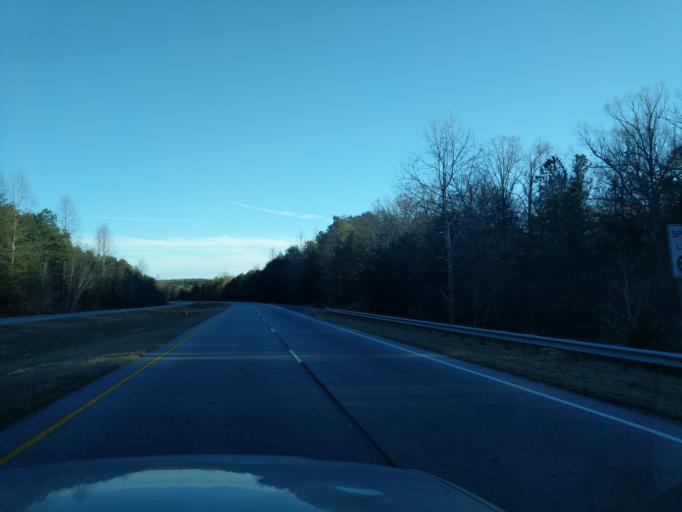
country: US
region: Georgia
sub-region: Stephens County
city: Toccoa
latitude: 34.5681
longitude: -83.3997
